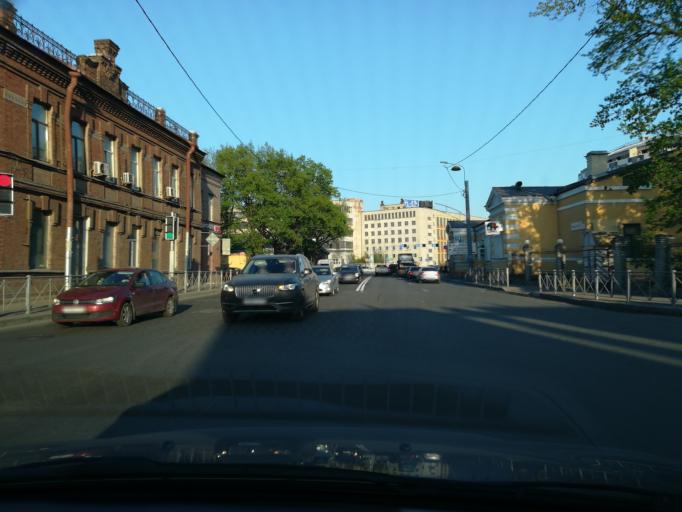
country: RU
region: St.-Petersburg
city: Vasyl'evsky Ostrov
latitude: 59.9528
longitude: 30.2627
